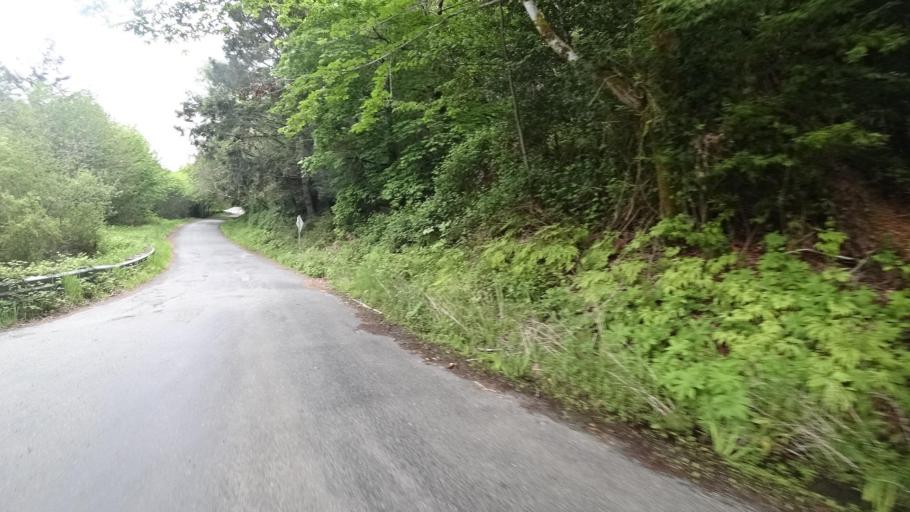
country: US
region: California
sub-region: Humboldt County
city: Willow Creek
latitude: 41.2073
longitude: -123.7582
